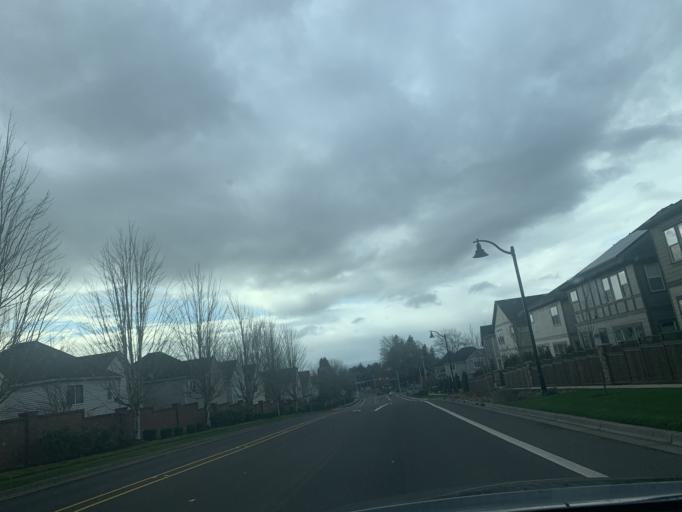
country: US
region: Oregon
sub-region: Washington County
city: Oak Hills
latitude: 45.5671
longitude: -122.8332
